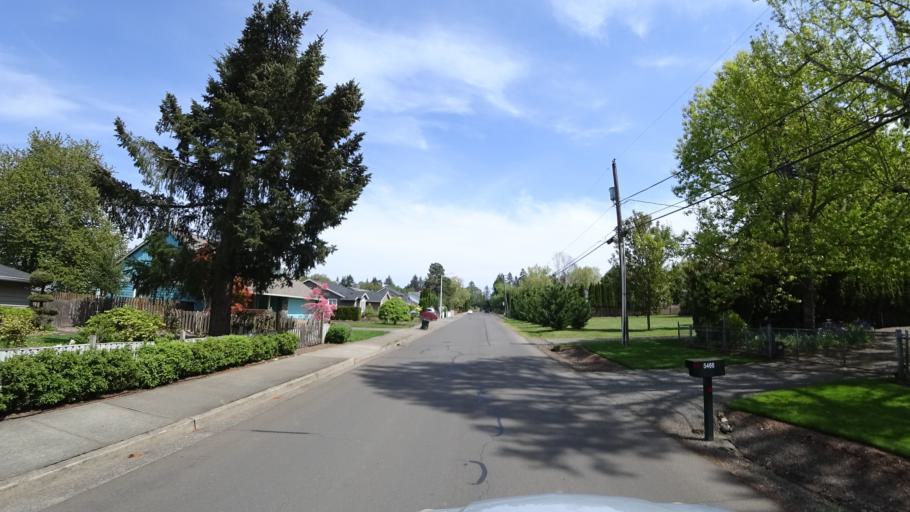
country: US
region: Oregon
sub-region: Washington County
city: Rockcreek
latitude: 45.5133
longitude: -122.9265
